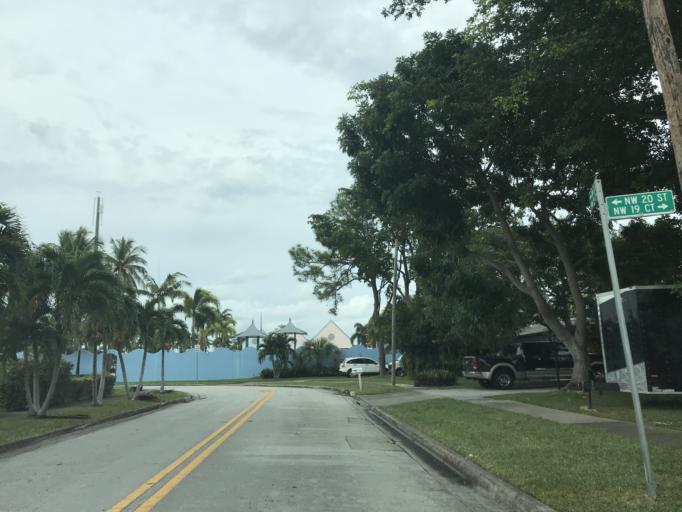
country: US
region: Florida
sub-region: Broward County
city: Margate
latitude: 26.2524
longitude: -80.2089
